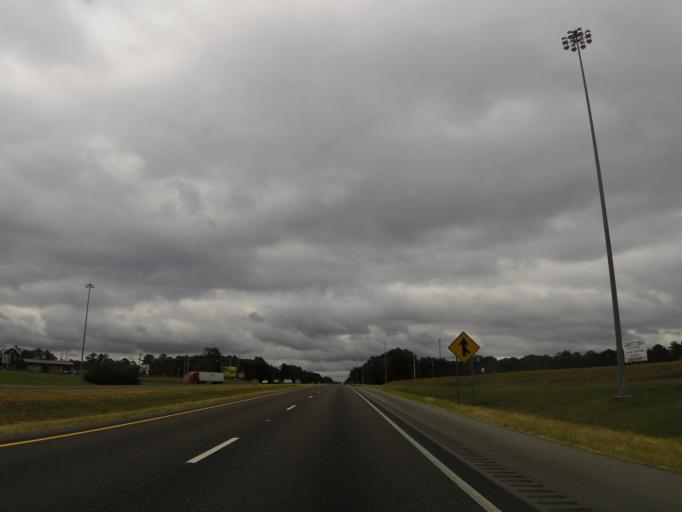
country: US
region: Alabama
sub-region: Conecuh County
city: Evergreen
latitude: 31.4582
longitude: -86.9648
